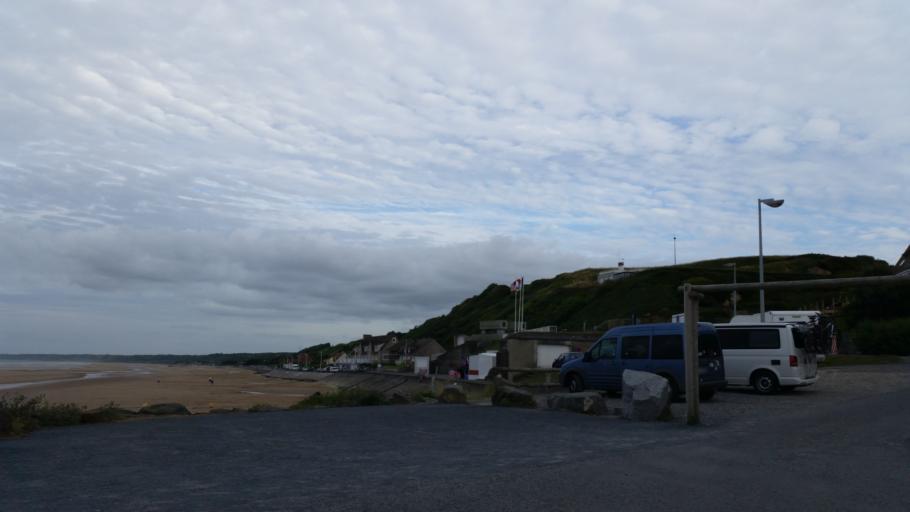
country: FR
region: Lower Normandy
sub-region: Departement du Calvados
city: Grandcamp-Maisy
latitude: 49.3801
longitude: -0.9039
